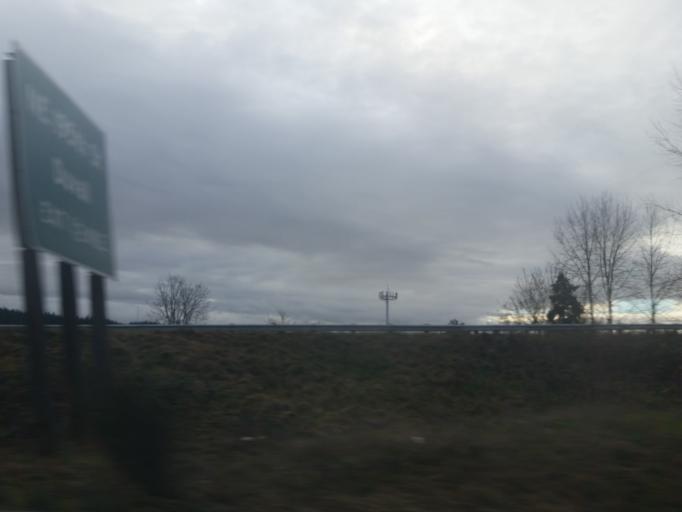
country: US
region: Washington
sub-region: King County
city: Woodinville
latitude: 47.7585
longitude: -122.1628
